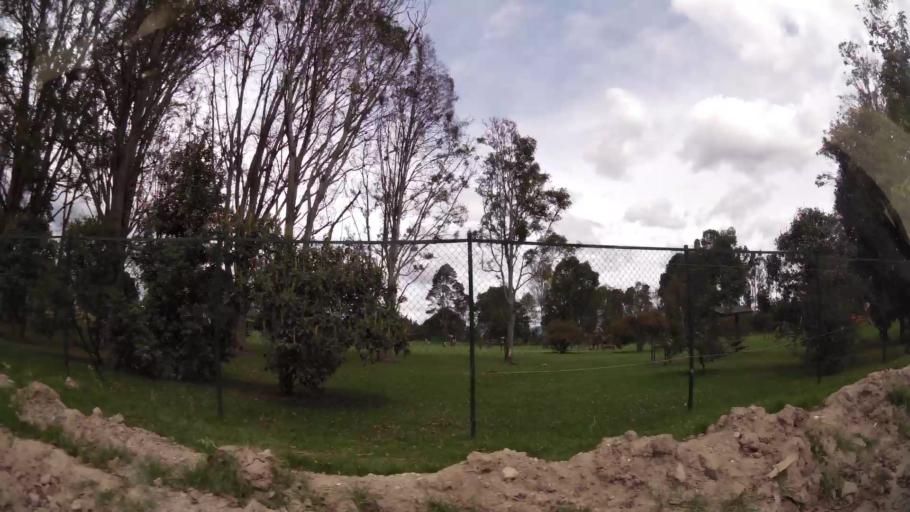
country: CO
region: Cundinamarca
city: Funza
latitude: 4.7314
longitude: -74.1477
